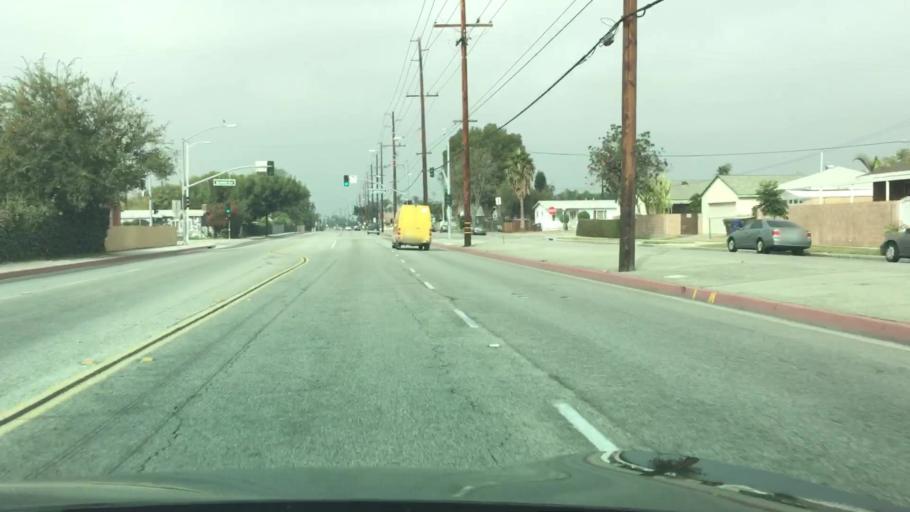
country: US
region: California
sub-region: Los Angeles County
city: West Puente Valley
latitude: 34.0452
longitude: -117.9742
